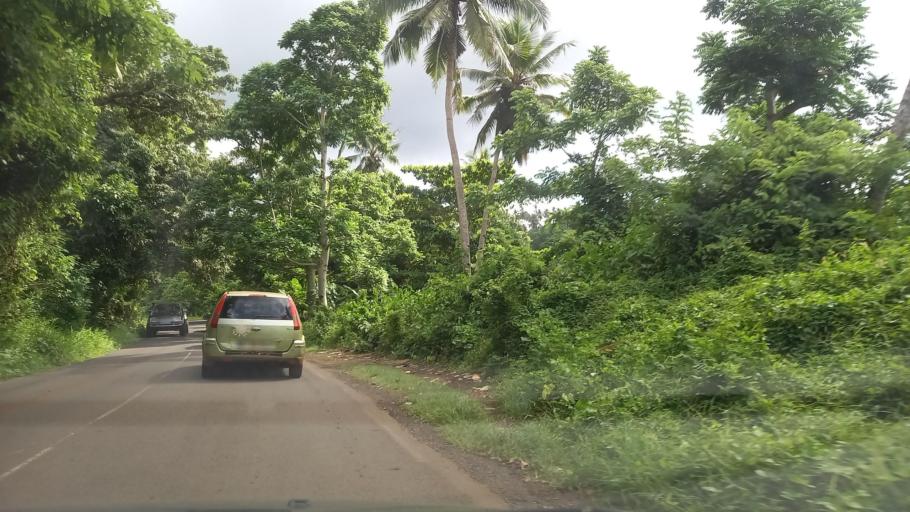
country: YT
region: Ouangani
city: Ouangani
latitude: -12.8406
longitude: 45.1242
